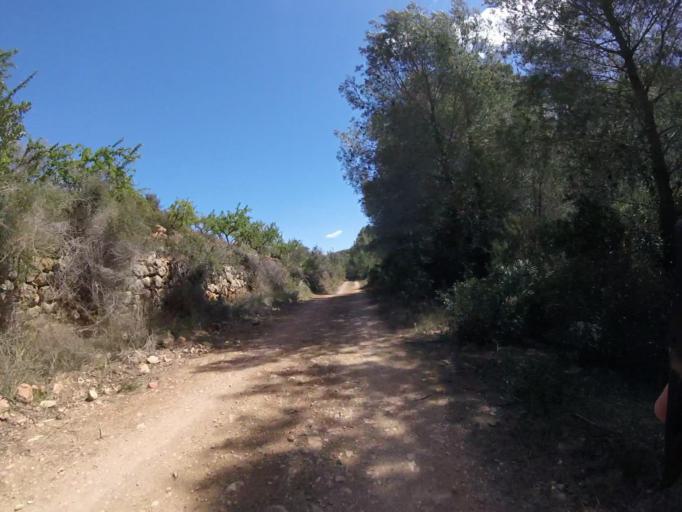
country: ES
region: Valencia
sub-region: Provincia de Castello
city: Orpesa/Oropesa del Mar
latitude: 40.1671
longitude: 0.1305
